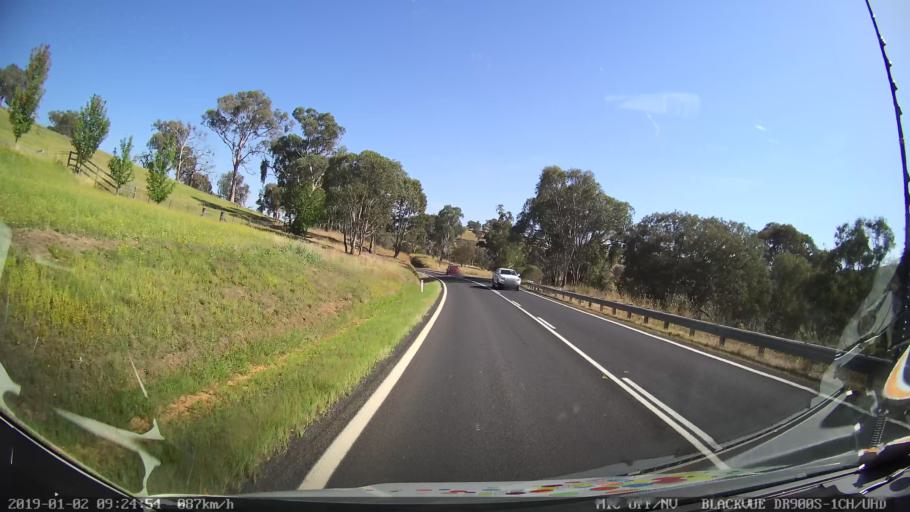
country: AU
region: New South Wales
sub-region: Tumut Shire
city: Tumut
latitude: -35.3709
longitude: 148.2920
